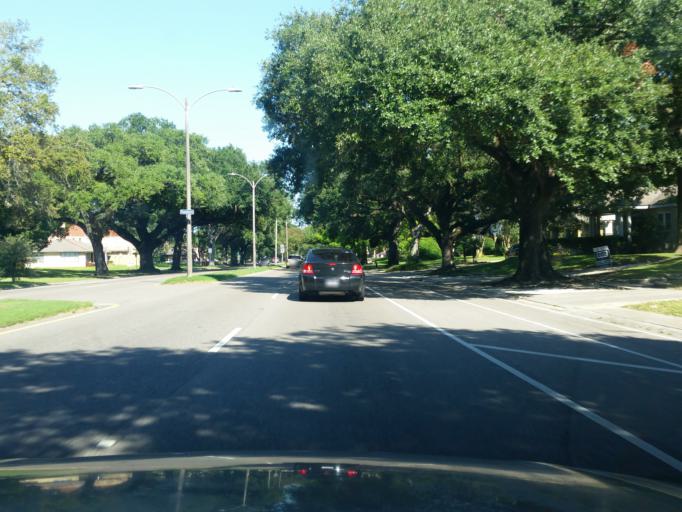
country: US
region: Louisiana
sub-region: Orleans Parish
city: New Orleans
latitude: 30.0029
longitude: -90.0524
